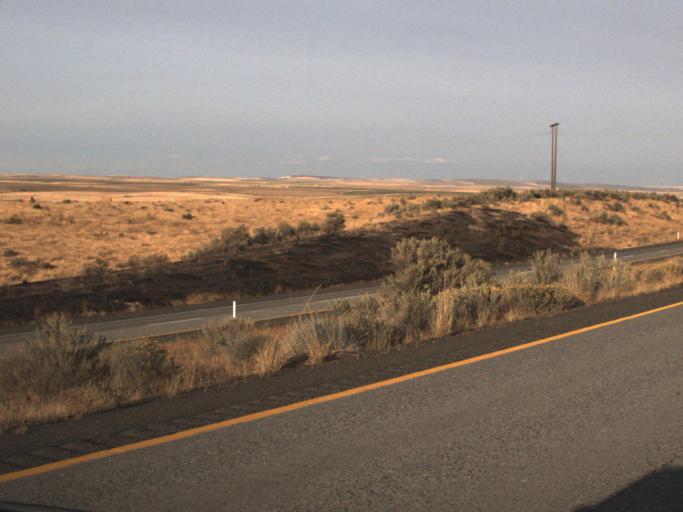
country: US
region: Oregon
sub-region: Umatilla County
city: Umatilla
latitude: 45.9841
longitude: -119.3116
